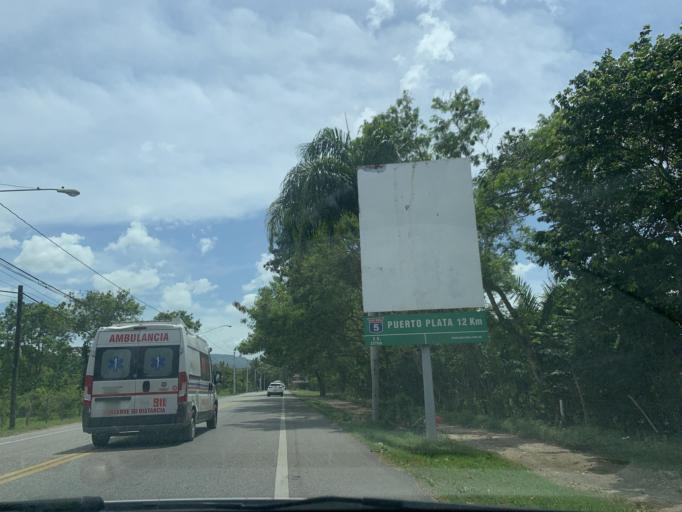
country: DO
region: Puerto Plata
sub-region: Puerto Plata
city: Puerto Plata
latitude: 19.7222
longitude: -70.6137
